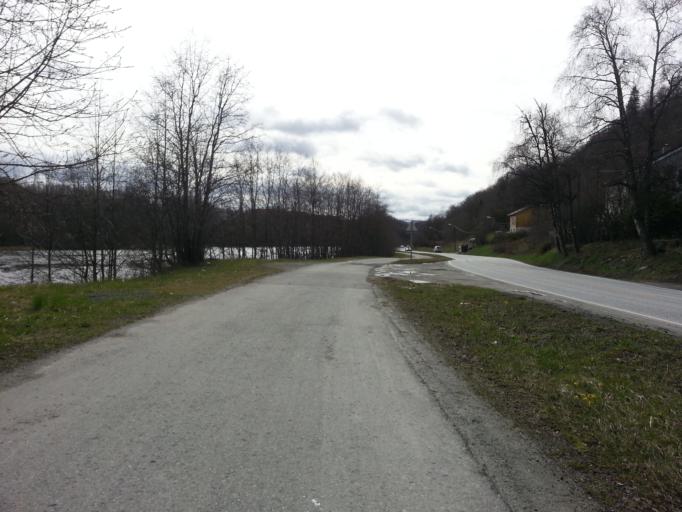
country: NO
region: Sor-Trondelag
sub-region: Trondheim
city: Trondheim
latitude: 63.4025
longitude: 10.3886
